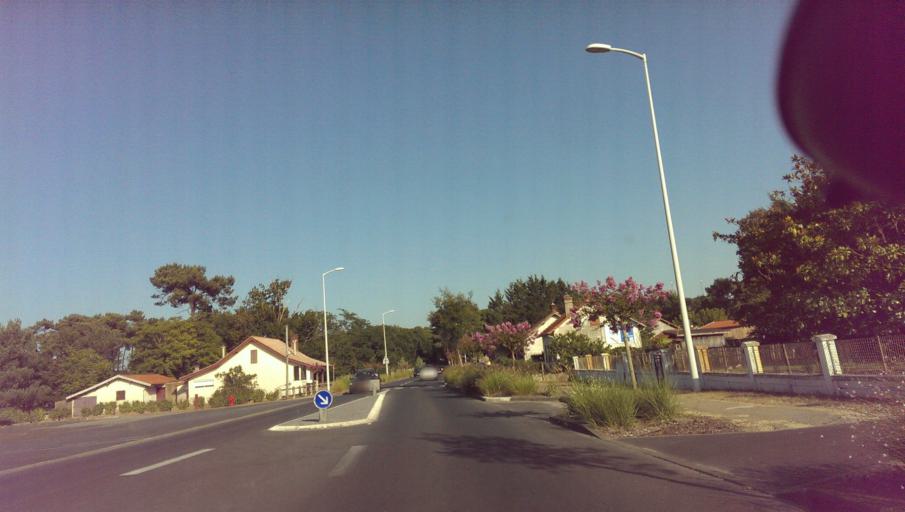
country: FR
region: Aquitaine
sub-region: Departement des Landes
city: Mimizan
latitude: 44.2073
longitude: -1.2423
